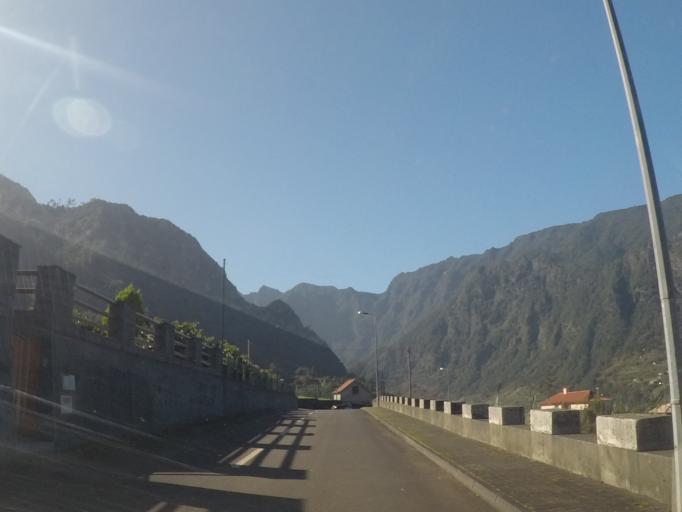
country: PT
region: Madeira
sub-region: Santana
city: Santana
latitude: 32.8012
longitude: -16.9595
